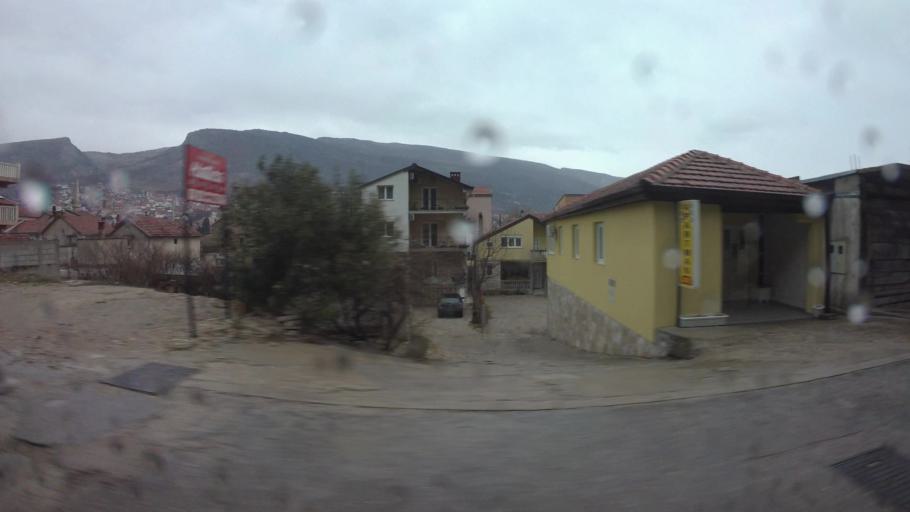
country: BA
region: Federation of Bosnia and Herzegovina
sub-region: Hercegovacko-Bosanski Kanton
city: Mostar
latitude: 43.3300
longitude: 17.8154
